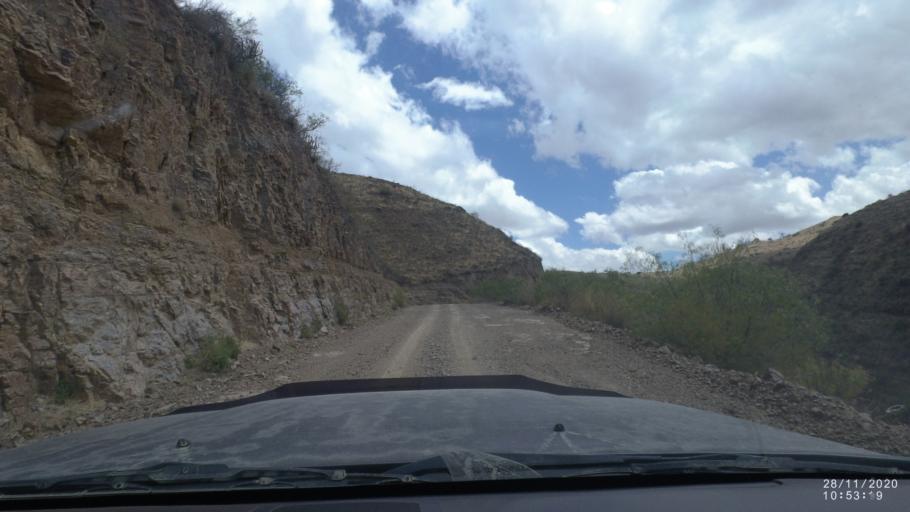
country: BO
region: Cochabamba
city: Capinota
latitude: -17.7819
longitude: -66.1190
